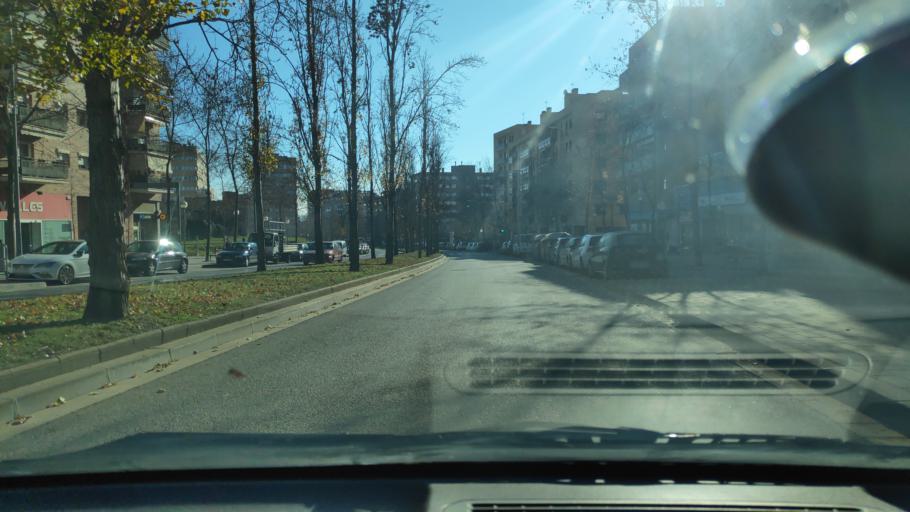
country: ES
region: Catalonia
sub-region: Provincia de Barcelona
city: Sant Quirze del Valles
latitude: 41.5629
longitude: 2.0818
